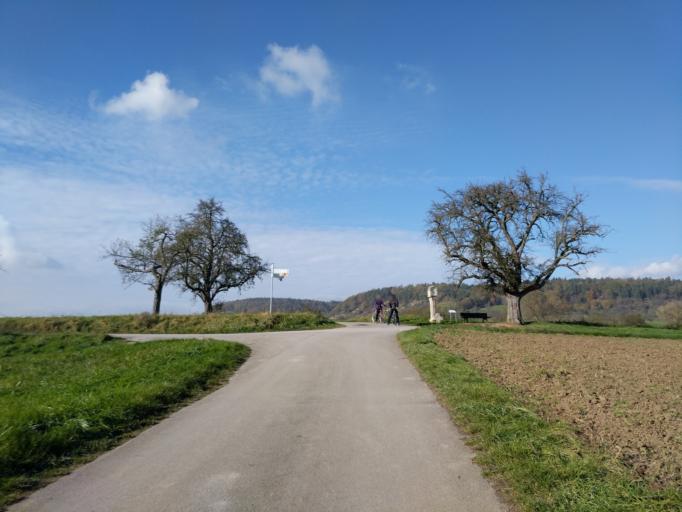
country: DE
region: Baden-Wuerttemberg
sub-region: Tuebingen Region
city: Rottenburg
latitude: 48.5065
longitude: 8.9596
